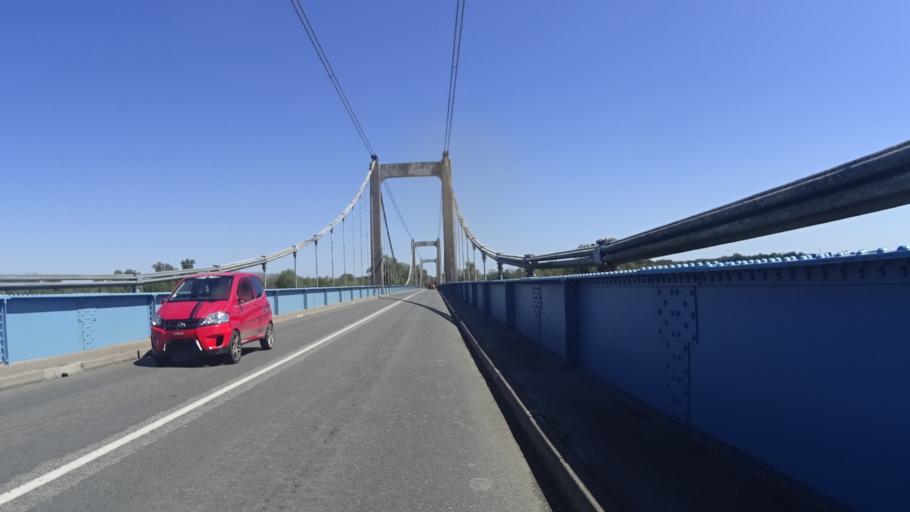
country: FR
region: Centre
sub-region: Departement du Loiret
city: Bonny-sur-Loire
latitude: 47.5499
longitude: 2.8340
